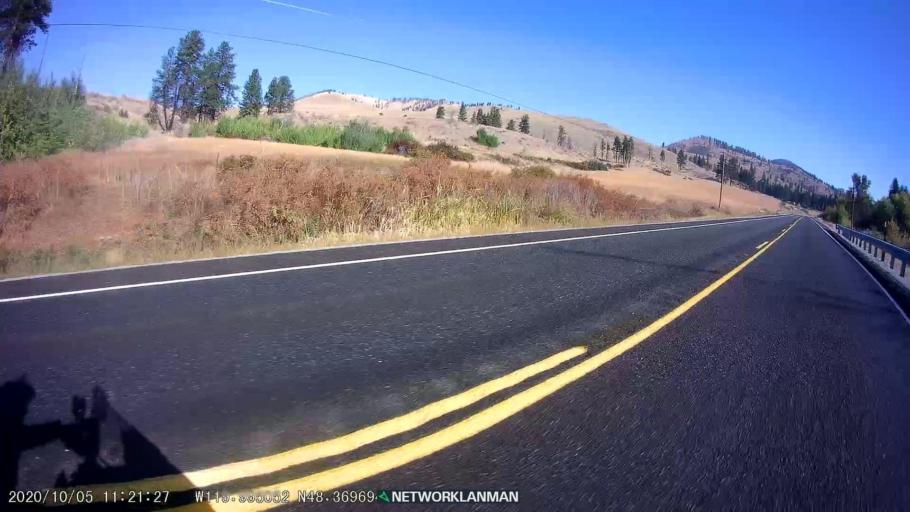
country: US
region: Washington
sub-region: Okanogan County
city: Brewster
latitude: 48.3694
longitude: -119.9947
